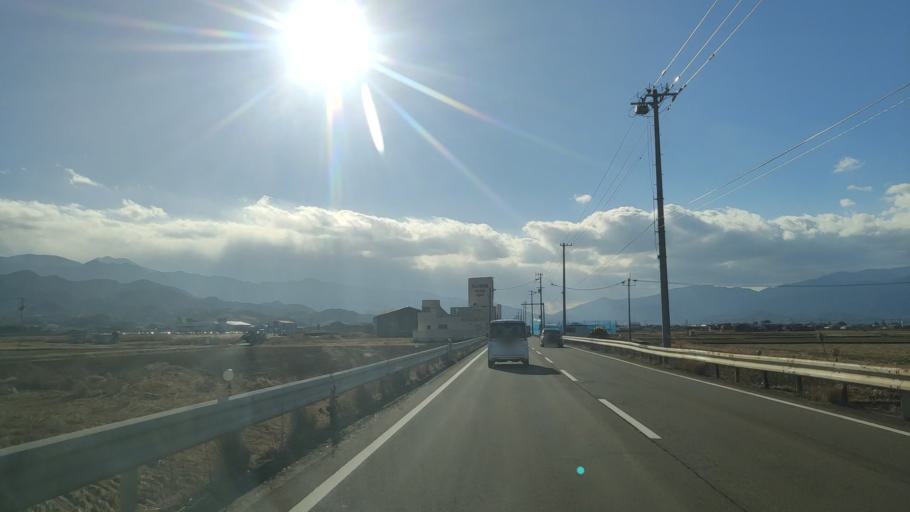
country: JP
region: Ehime
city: Saijo
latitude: 33.9156
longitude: 133.1192
